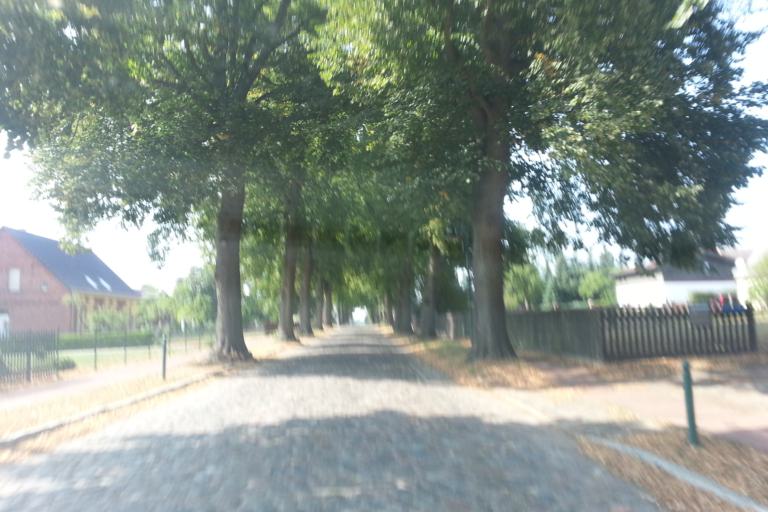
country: DE
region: Mecklenburg-Vorpommern
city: Strasburg
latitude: 53.6117
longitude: 13.7800
